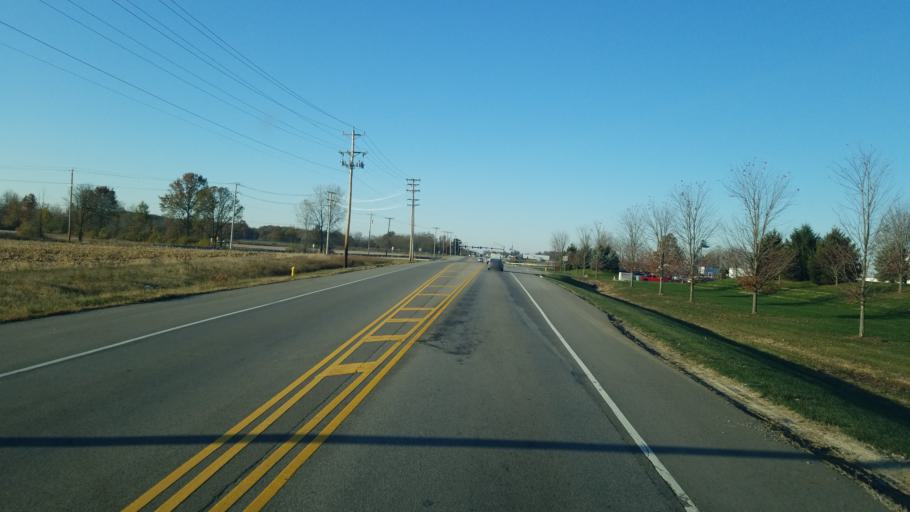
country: US
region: Ohio
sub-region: Delaware County
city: Delaware
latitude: 40.2744
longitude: -83.1029
